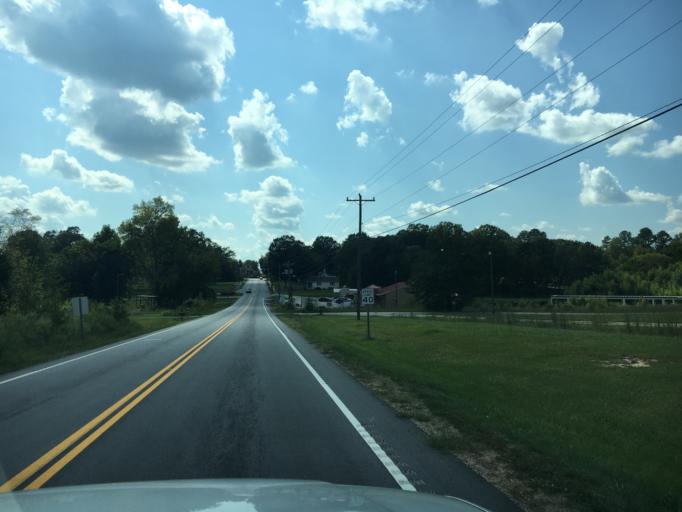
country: US
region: South Carolina
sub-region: Greenville County
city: Fountain Inn
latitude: 34.6100
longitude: -82.1089
